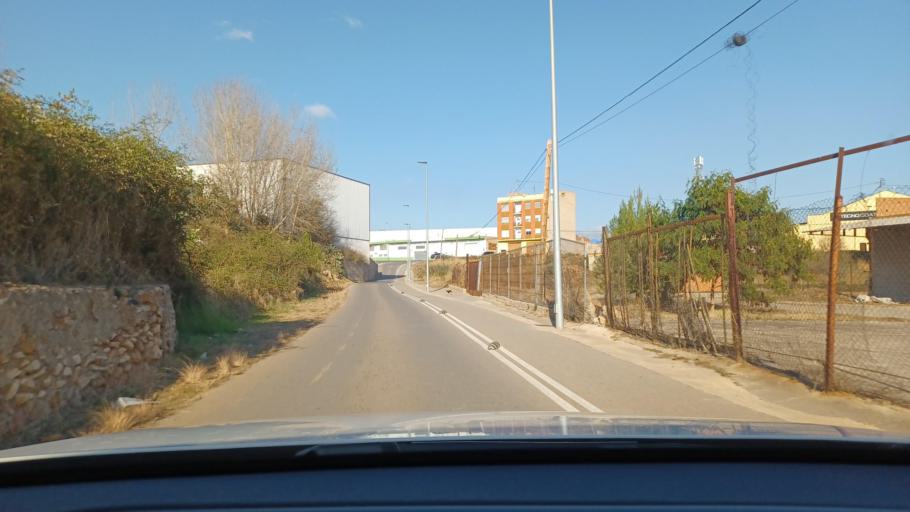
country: ES
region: Valencia
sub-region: Provincia de Castello
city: Onda
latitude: 39.9629
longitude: -0.2526
